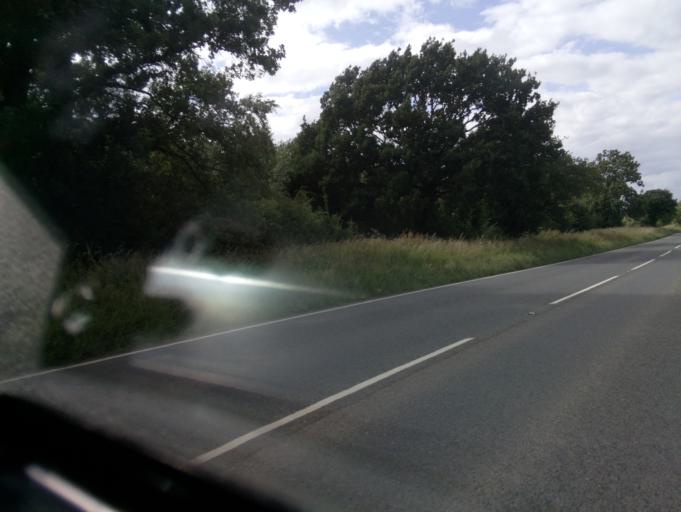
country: GB
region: England
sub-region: Leicestershire
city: Measham
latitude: 52.6695
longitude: -1.5395
